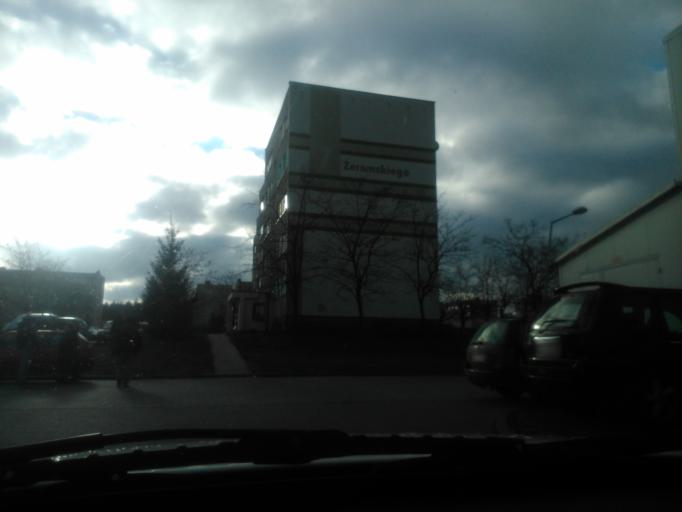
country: PL
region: Kujawsko-Pomorskie
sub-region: Powiat golubsko-dobrzynski
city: Golub-Dobrzyn
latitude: 53.1031
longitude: 19.0529
